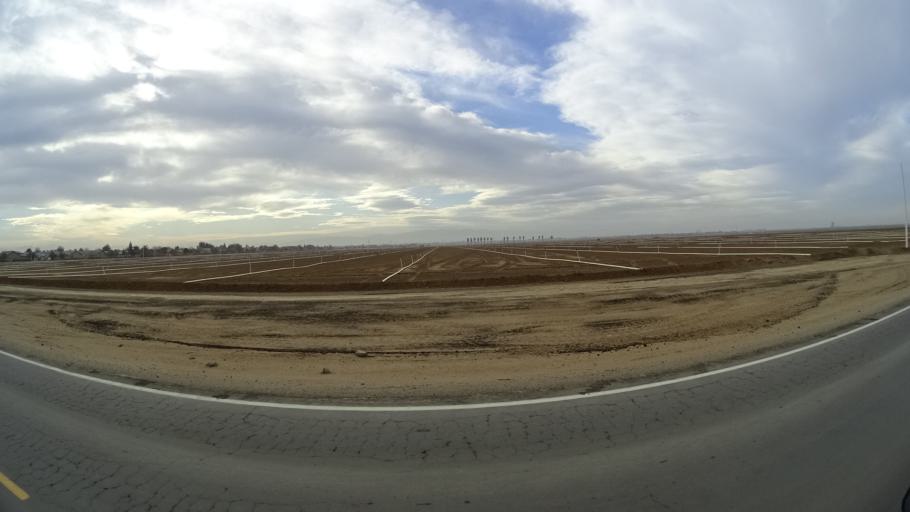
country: US
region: California
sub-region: Kern County
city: Rosedale
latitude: 35.4198
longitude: -119.1563
